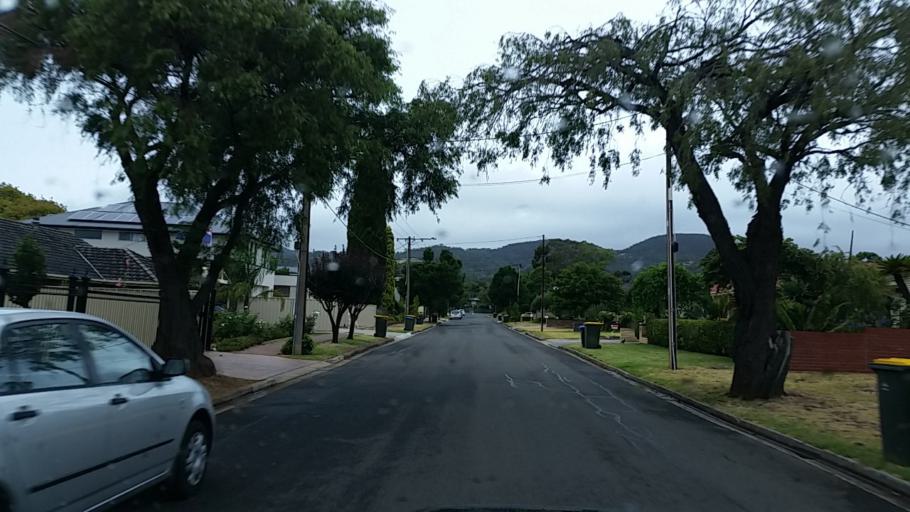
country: AU
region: South Australia
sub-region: Campbelltown
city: Campbelltown
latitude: -34.8953
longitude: 138.6824
